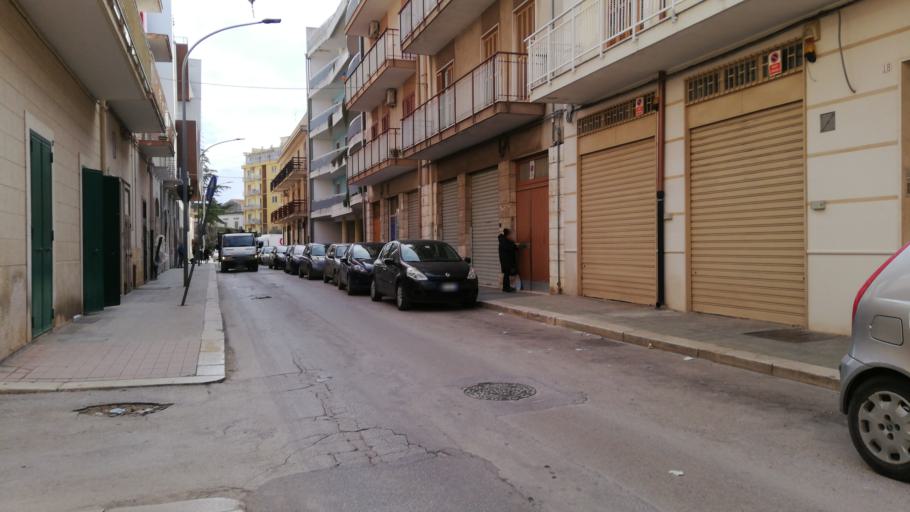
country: IT
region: Apulia
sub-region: Provincia di Bari
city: Bitonto
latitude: 41.1071
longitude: 16.6846
